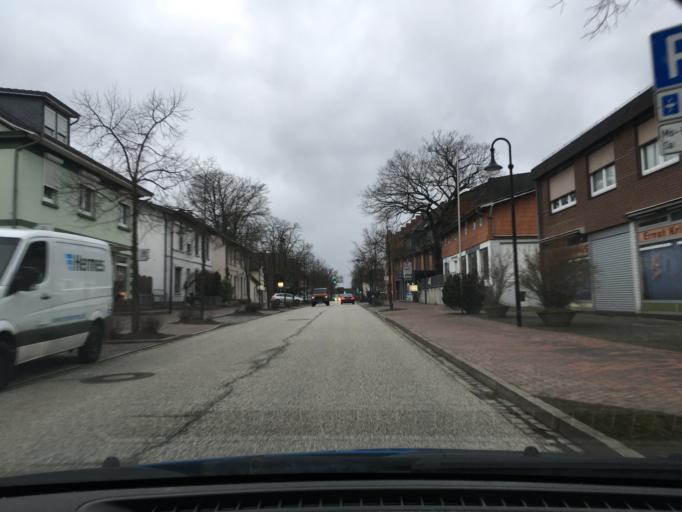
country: DE
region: Schleswig-Holstein
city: Schwarzenbek
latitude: 53.5014
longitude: 10.4850
